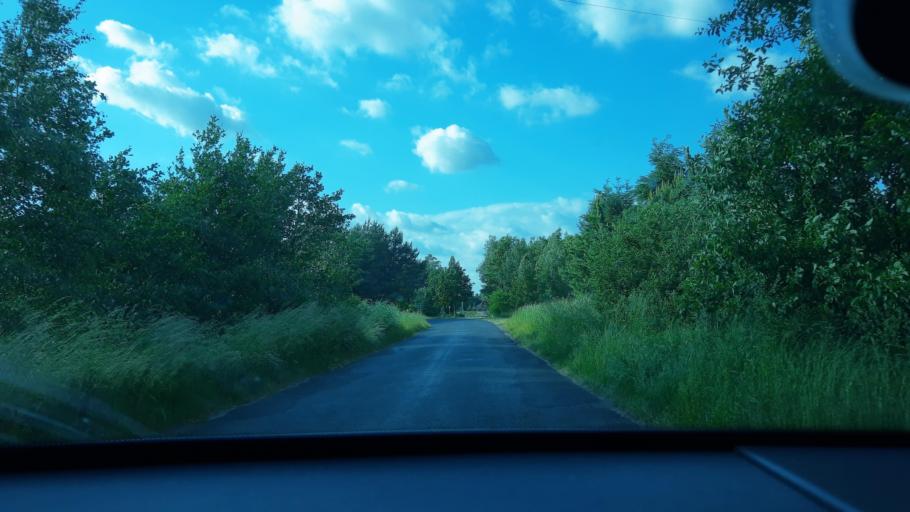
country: PL
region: Lodz Voivodeship
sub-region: Powiat zdunskowolski
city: Zapolice
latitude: 51.5327
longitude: 18.8369
